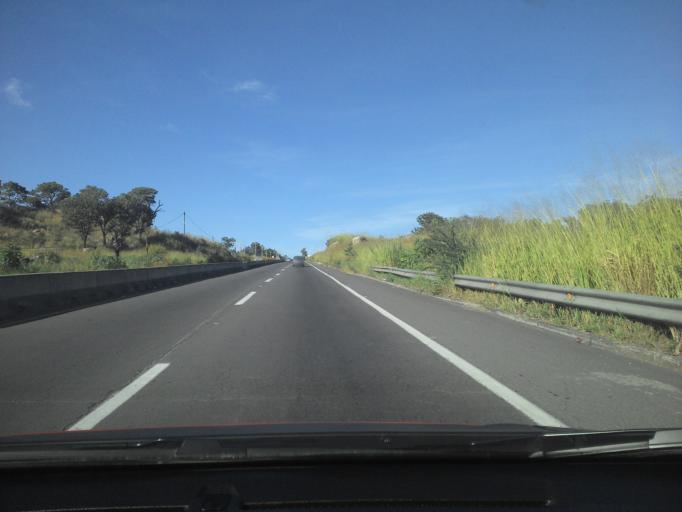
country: MX
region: Jalisco
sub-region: Tala
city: Los Ruisenores
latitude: 20.6915
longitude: -103.6918
